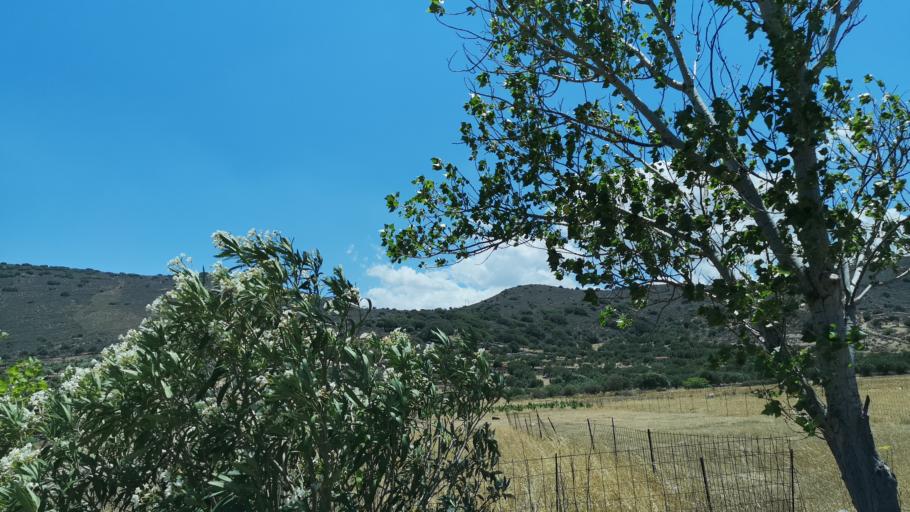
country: GR
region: Crete
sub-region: Nomos Lasithiou
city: Neapoli
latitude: 35.2584
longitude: 25.6549
